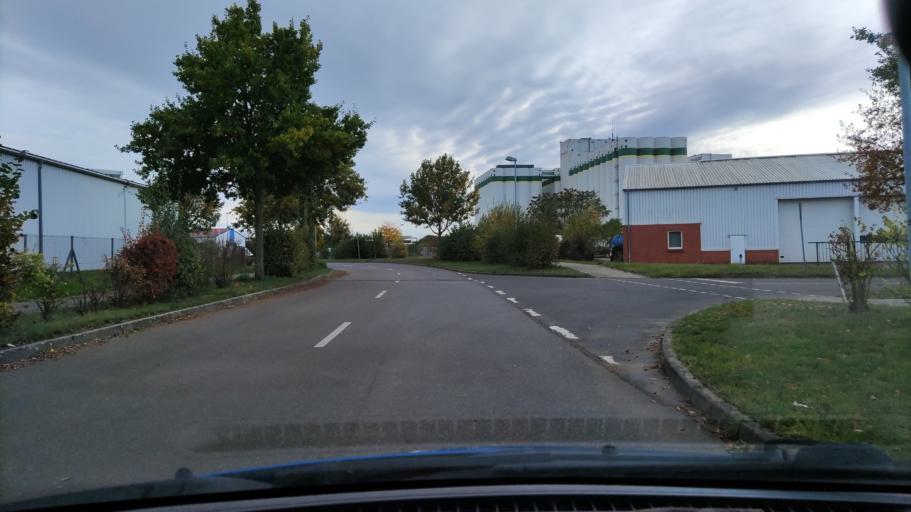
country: DE
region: Brandenburg
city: Karstadt
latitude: 53.1696
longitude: 11.7419
